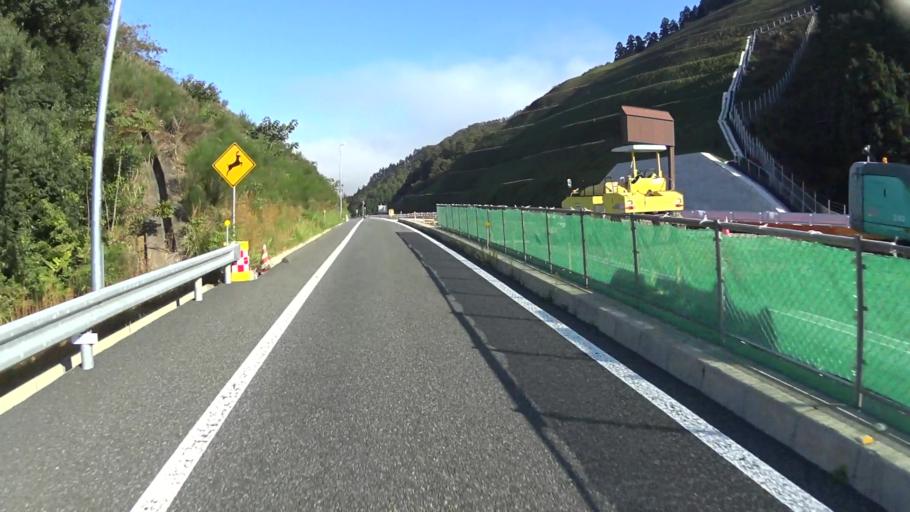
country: JP
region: Kyoto
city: Ayabe
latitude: 35.2824
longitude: 135.3370
